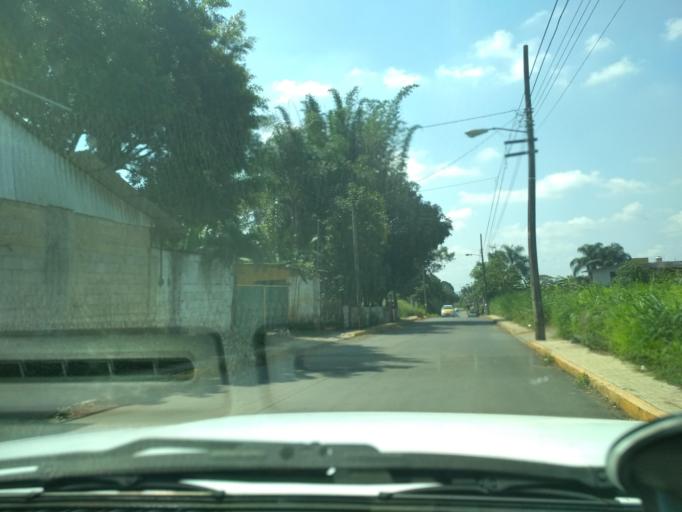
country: MX
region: Veracruz
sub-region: Fortin
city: Fraccionamiento los Alamos
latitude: 18.9157
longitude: -96.9745
